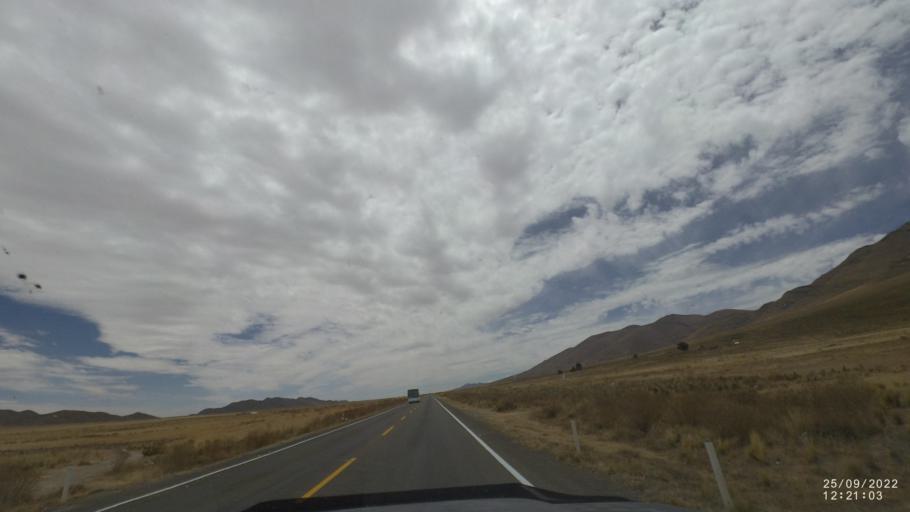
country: BO
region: Oruro
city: Poopo
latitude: -18.4194
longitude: -66.9750
